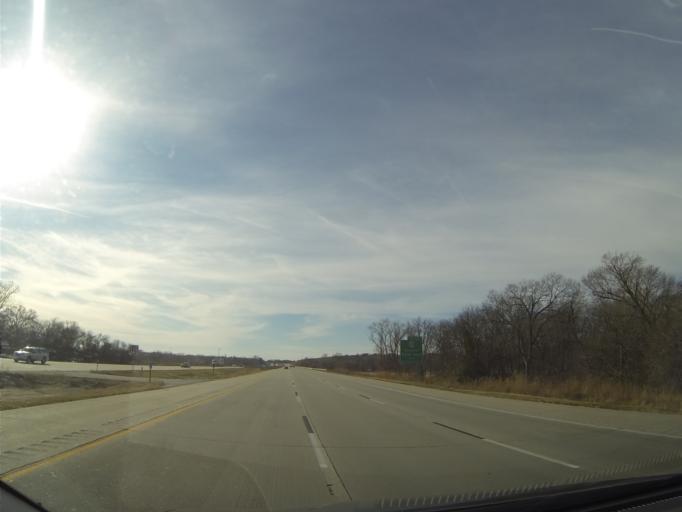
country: US
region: Nebraska
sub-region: Saunders County
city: Ashland
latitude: 41.0309
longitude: -96.2934
